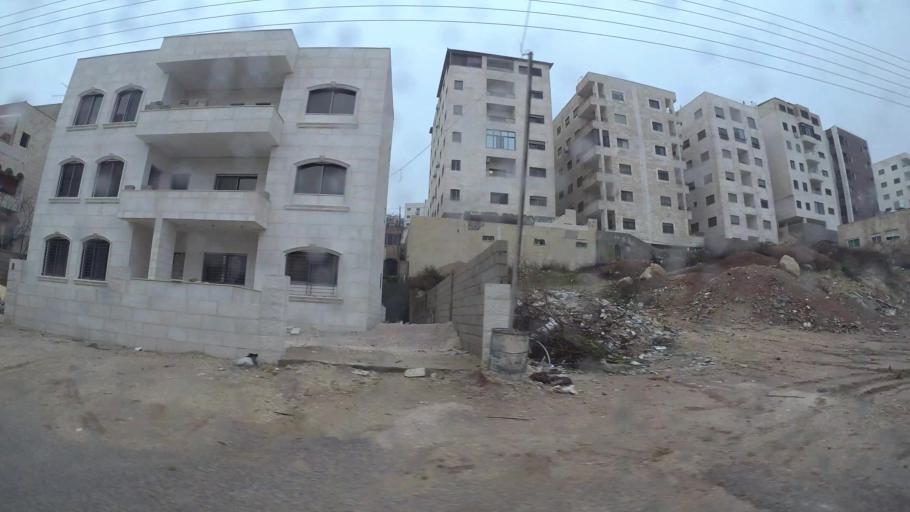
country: JO
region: Amman
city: Al Jubayhah
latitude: 32.0352
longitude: 35.8518
